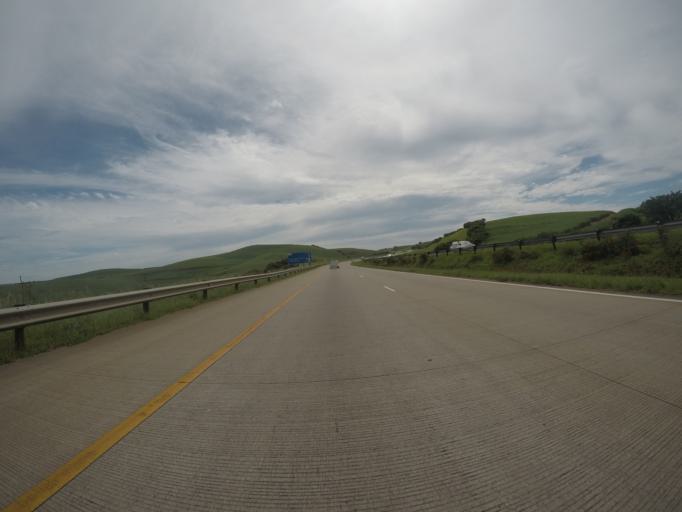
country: ZA
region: KwaZulu-Natal
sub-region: iLembe District Municipality
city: Ballitoville
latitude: -29.4391
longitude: 31.2619
